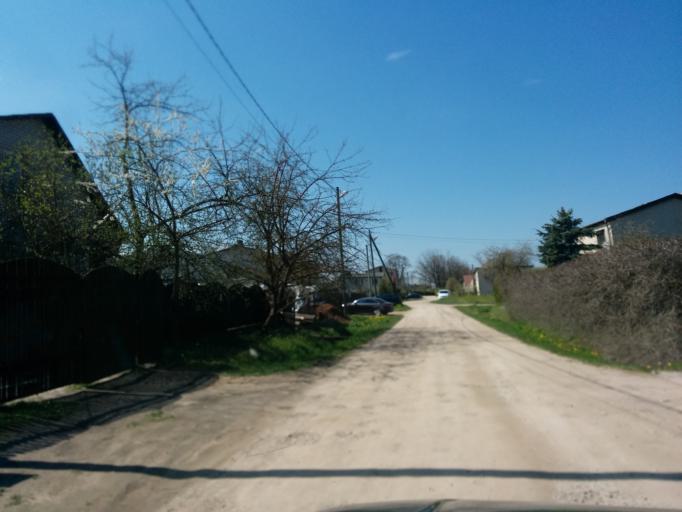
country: LV
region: Jelgava
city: Jelgava
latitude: 56.6231
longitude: 23.7372
